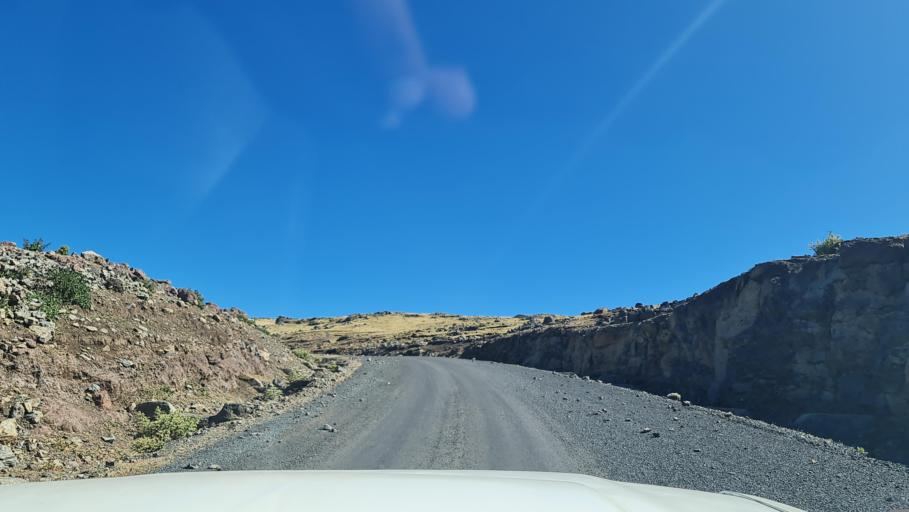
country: ET
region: Amhara
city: Debark'
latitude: 13.1498
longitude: 38.1870
